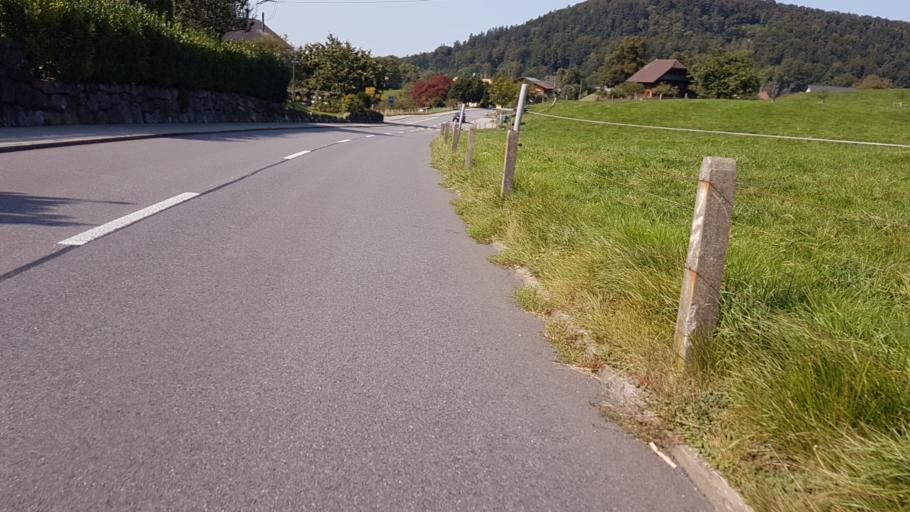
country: CH
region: Bern
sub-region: Frutigen-Niedersimmental District
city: Aeschi
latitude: 46.6679
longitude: 7.6816
